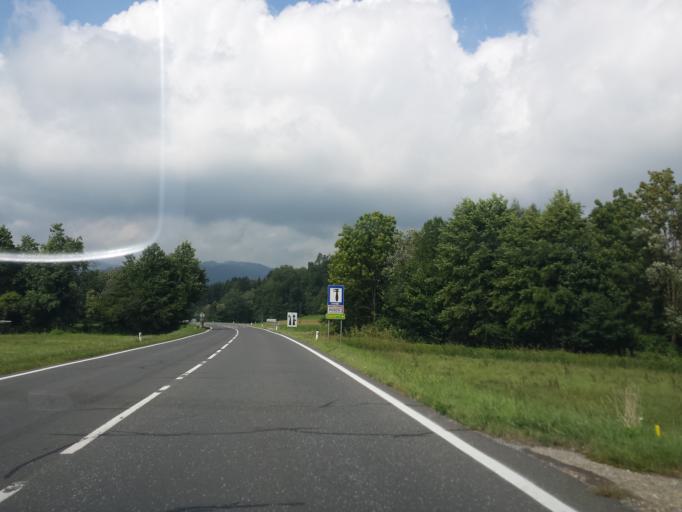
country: AT
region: Styria
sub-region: Politischer Bezirk Deutschlandsberg
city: Deutschlandsberg
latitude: 46.8314
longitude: 15.2489
